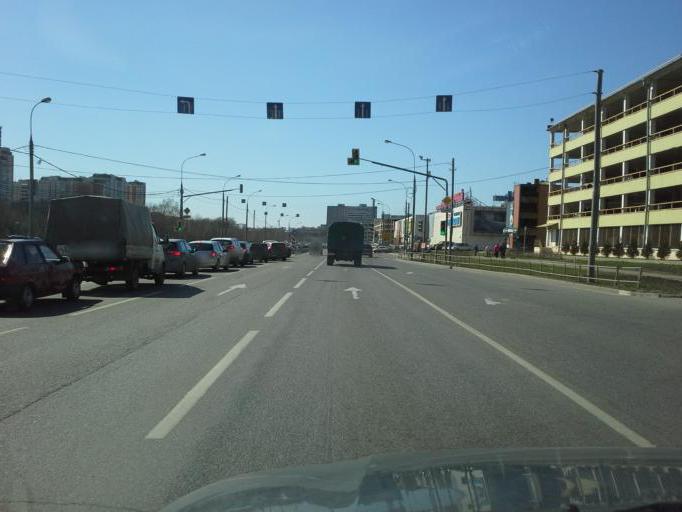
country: RU
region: Moskovskaya
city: Zarech'ye
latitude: 55.6592
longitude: 37.4056
